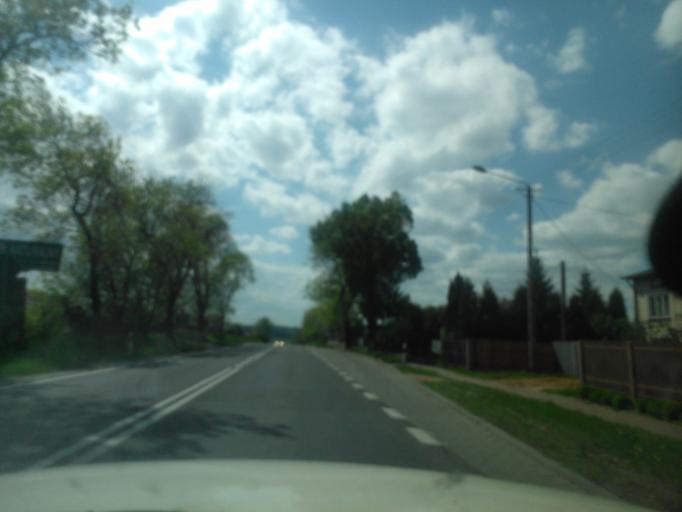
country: PL
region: Swietokrzyskie
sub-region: Powiat ostrowiecki
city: Kunow
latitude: 50.9492
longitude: 21.3125
